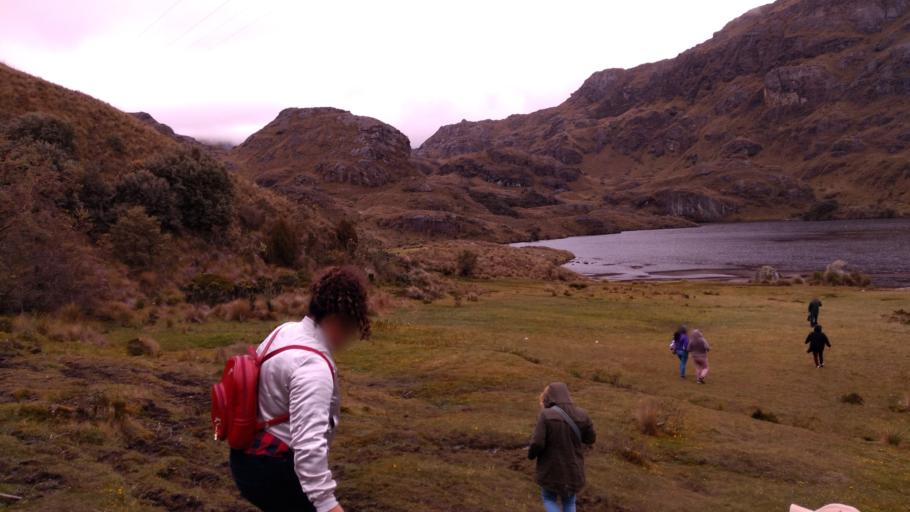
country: EC
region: Azuay
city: Cuenca
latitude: -2.7828
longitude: -79.2247
